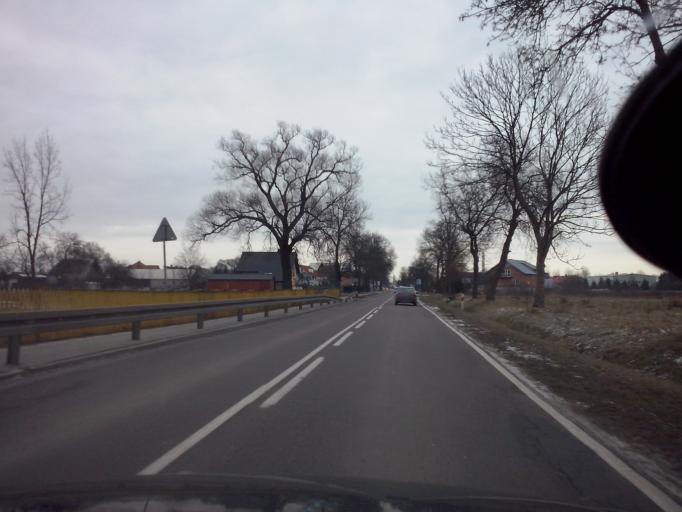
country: PL
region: Lublin Voivodeship
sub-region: Powiat bilgorajski
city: Bilgoraj
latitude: 50.5206
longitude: 22.6826
